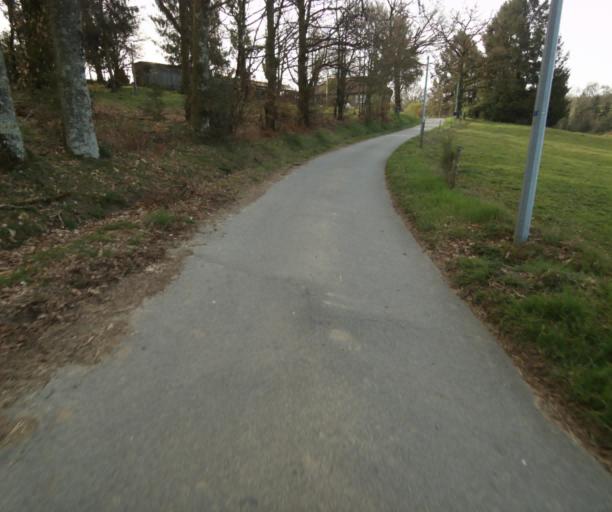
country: FR
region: Limousin
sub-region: Departement de la Correze
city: Chamboulive
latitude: 45.4418
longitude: 1.7578
